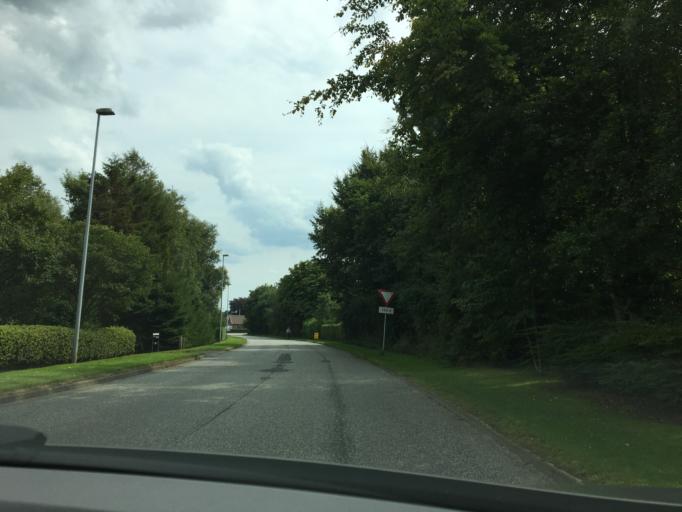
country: DK
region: Central Jutland
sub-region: Viborg Kommune
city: Stoholm
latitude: 56.4892
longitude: 9.1400
